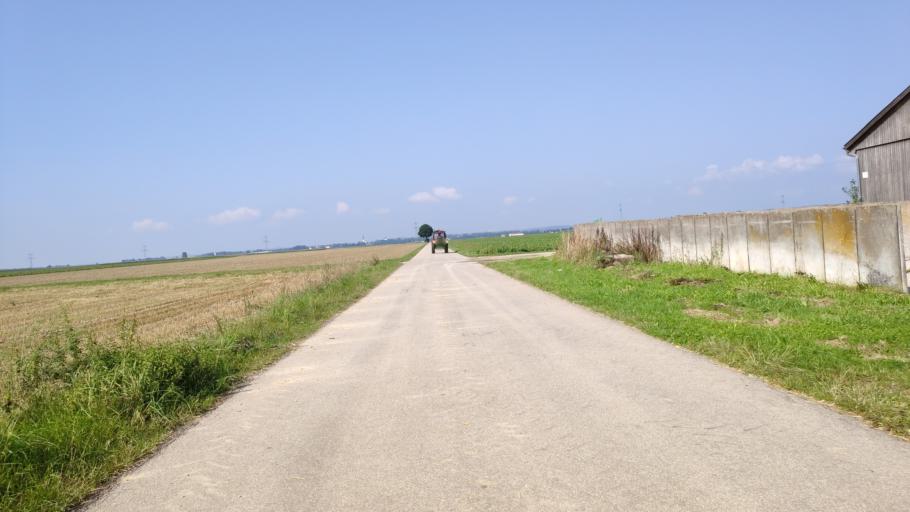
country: DE
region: Bavaria
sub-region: Swabia
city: Graben
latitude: 48.1865
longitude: 10.8114
